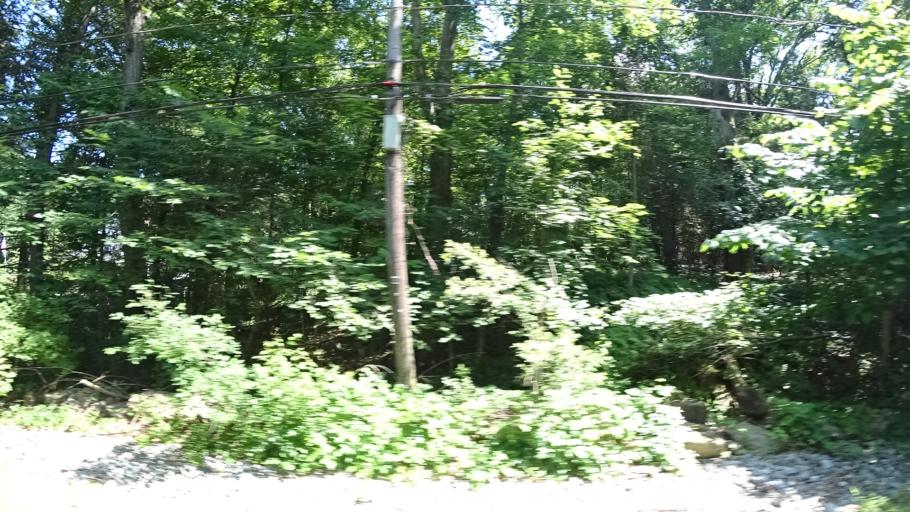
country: US
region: Massachusetts
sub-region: Norfolk County
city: Dedham
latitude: 42.2506
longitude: -71.1975
